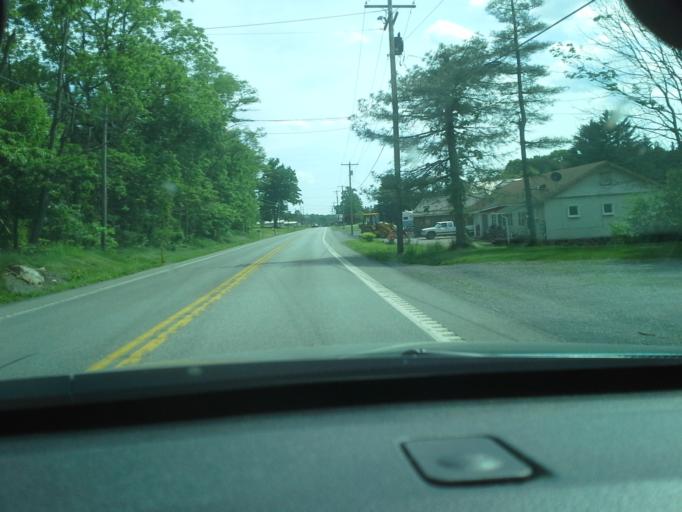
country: US
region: Pennsylvania
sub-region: Fulton County
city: McConnellsburg
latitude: 39.9681
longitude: -77.9752
